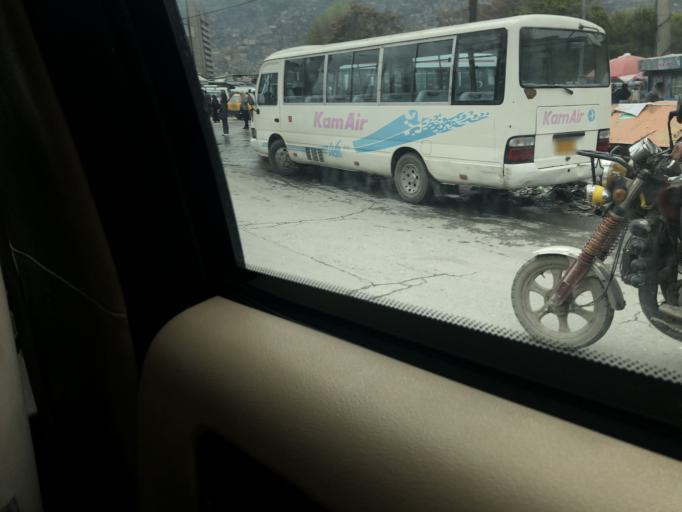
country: AF
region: Kabul
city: Kabul
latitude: 34.5160
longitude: 69.1708
